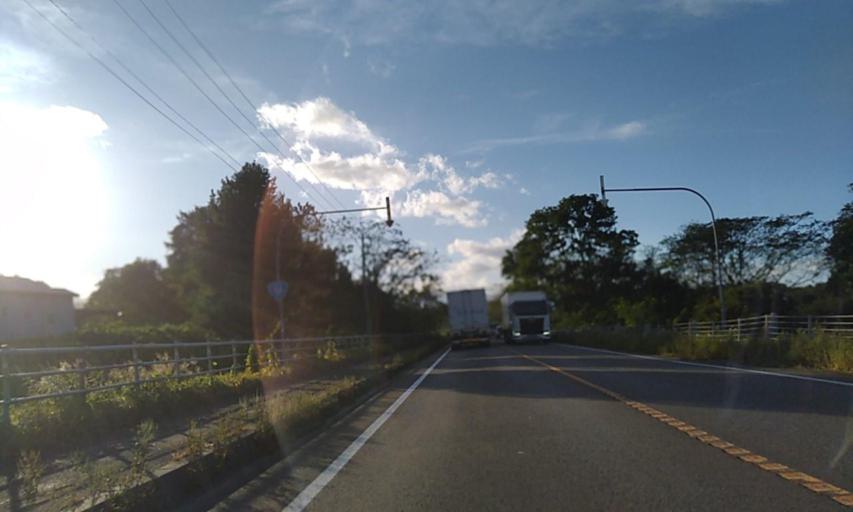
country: JP
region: Hokkaido
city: Otofuke
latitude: 42.9479
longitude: 142.9386
